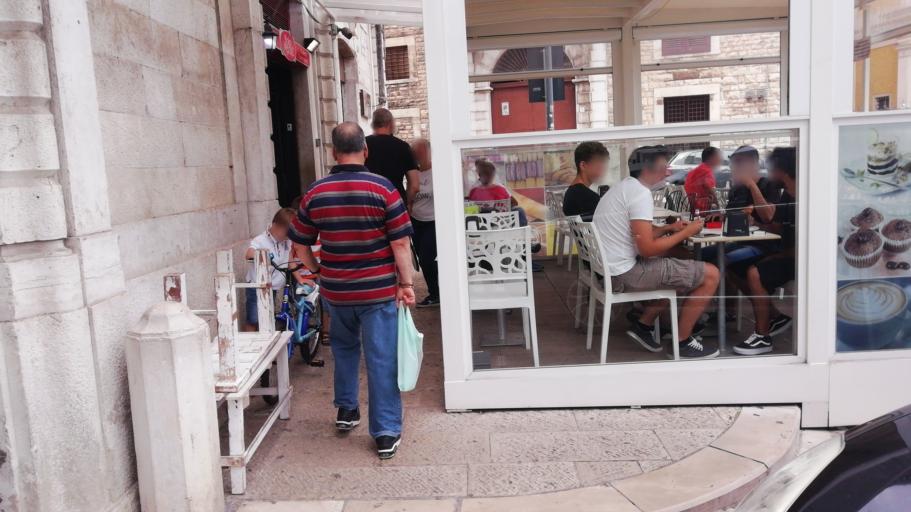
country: IT
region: Apulia
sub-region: Provincia di Barletta - Andria - Trani
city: Andria
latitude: 41.2256
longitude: 16.2971
